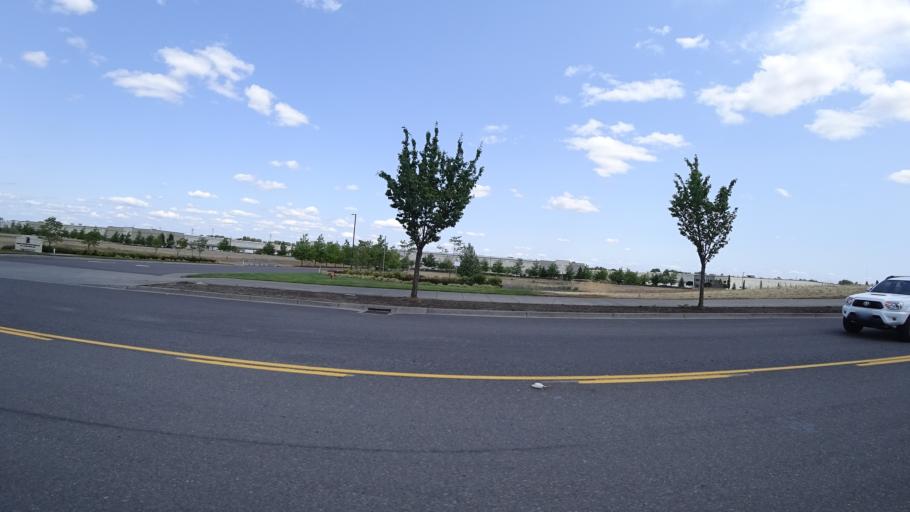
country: US
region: Washington
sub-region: Clark County
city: Lake Shore
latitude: 45.6273
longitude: -122.7718
